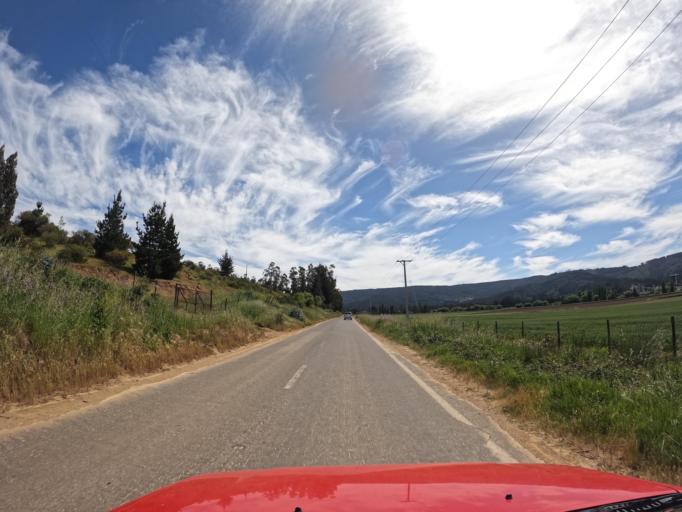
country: CL
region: Maule
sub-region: Provincia de Talca
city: Constitucion
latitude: -34.9942
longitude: -72.0143
